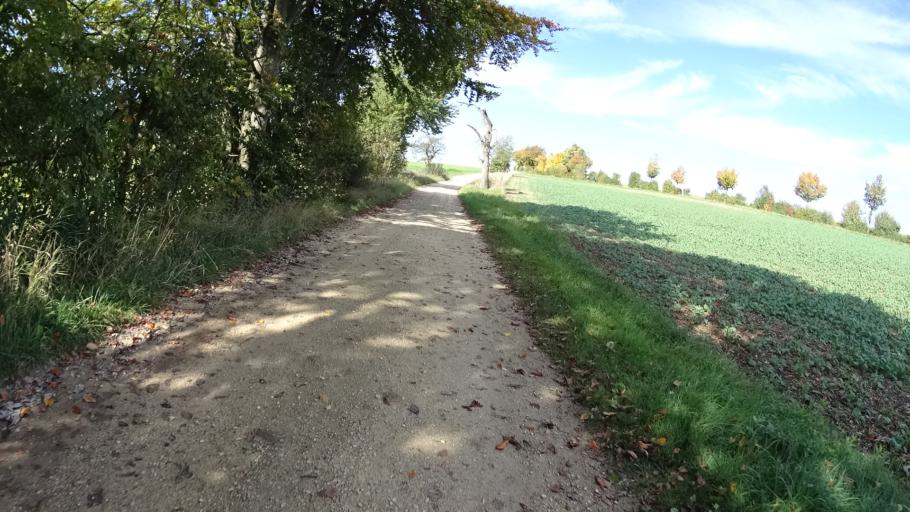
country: DE
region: Bavaria
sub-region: Upper Bavaria
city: Bohmfeld
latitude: 48.8512
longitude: 11.3714
